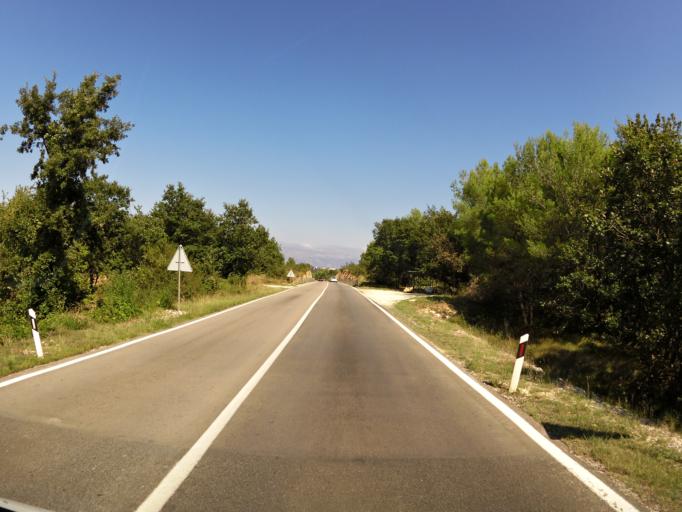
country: HR
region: Zadarska
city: Policnik
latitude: 44.1604
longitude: 15.3461
